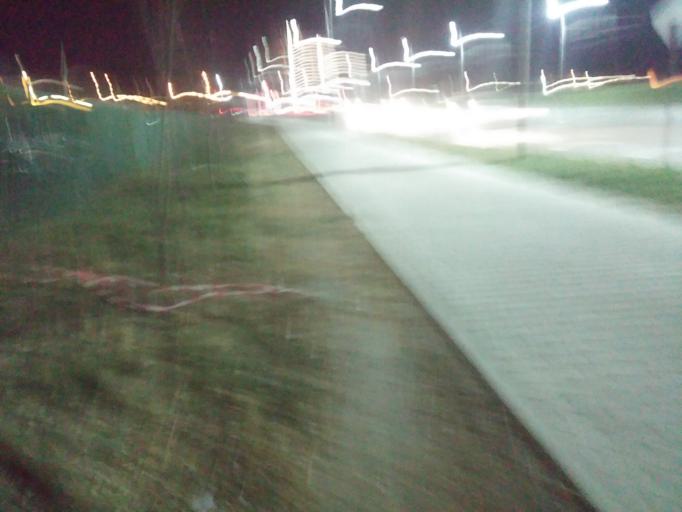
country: RU
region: Khabarovsk Krai
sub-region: Khabarovskiy Rayon
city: Khabarovsk
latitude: 48.4540
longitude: 135.0958
